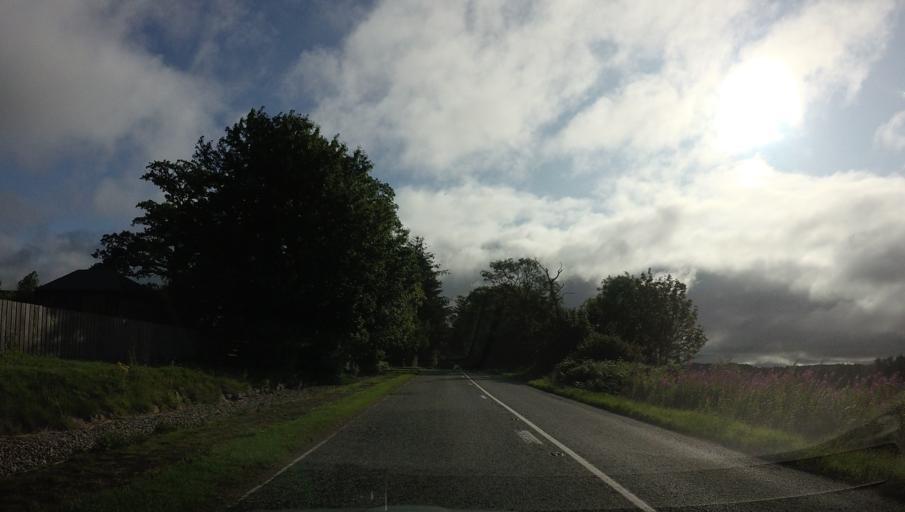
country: GB
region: Scotland
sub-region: Aberdeenshire
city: Banchory
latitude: 57.0636
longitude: -2.3904
